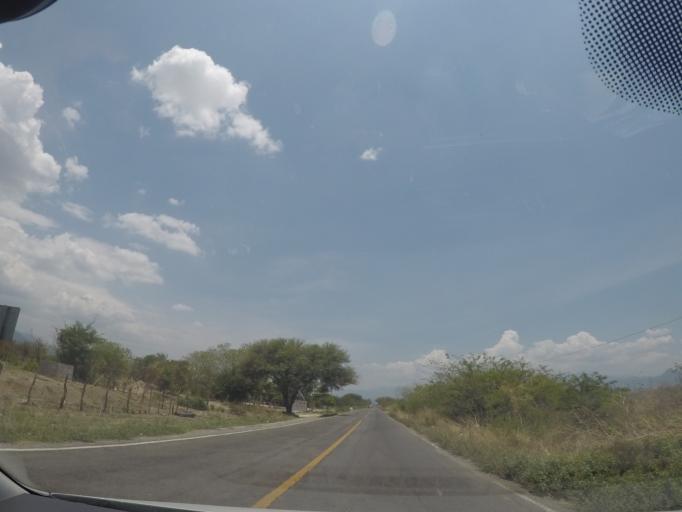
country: MX
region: Oaxaca
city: Santa Maria Jalapa del Marques
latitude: 16.4398
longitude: -95.4682
